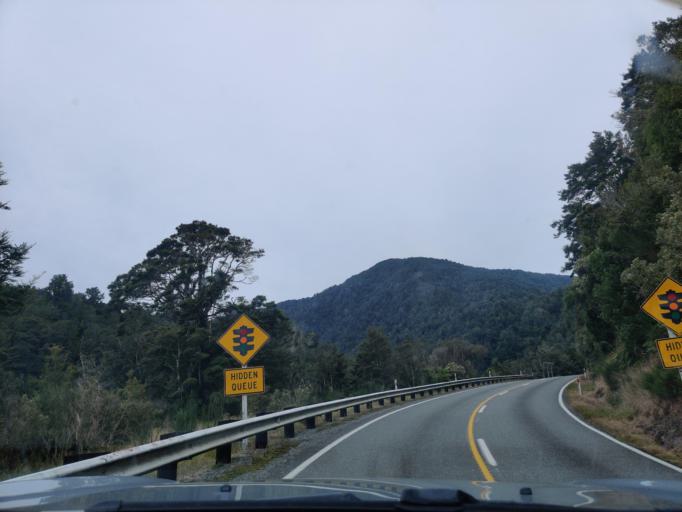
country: NZ
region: West Coast
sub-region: Buller District
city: Westport
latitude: -41.8470
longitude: 171.7406
